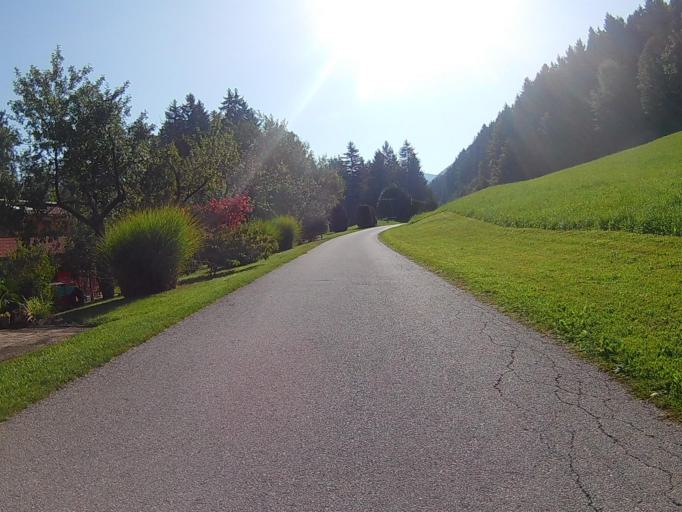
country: SI
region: Slovenj Gradec
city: Legen
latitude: 46.4450
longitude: 15.1815
